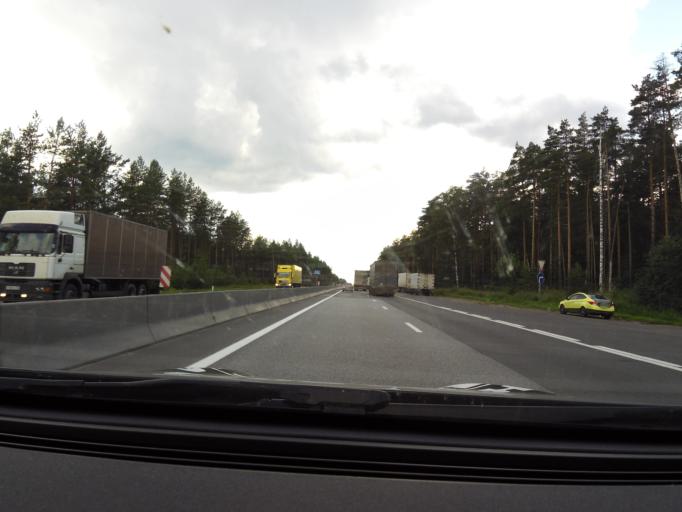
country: RU
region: Nizjnij Novgorod
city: Yuganets
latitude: 56.2879
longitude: 43.2285
